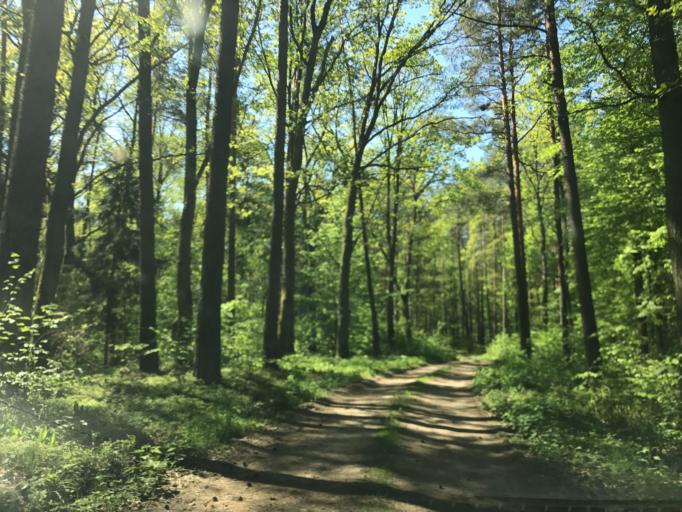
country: PL
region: Warmian-Masurian Voivodeship
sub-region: Powiat dzialdowski
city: Lidzbark
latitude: 53.2580
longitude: 19.7523
